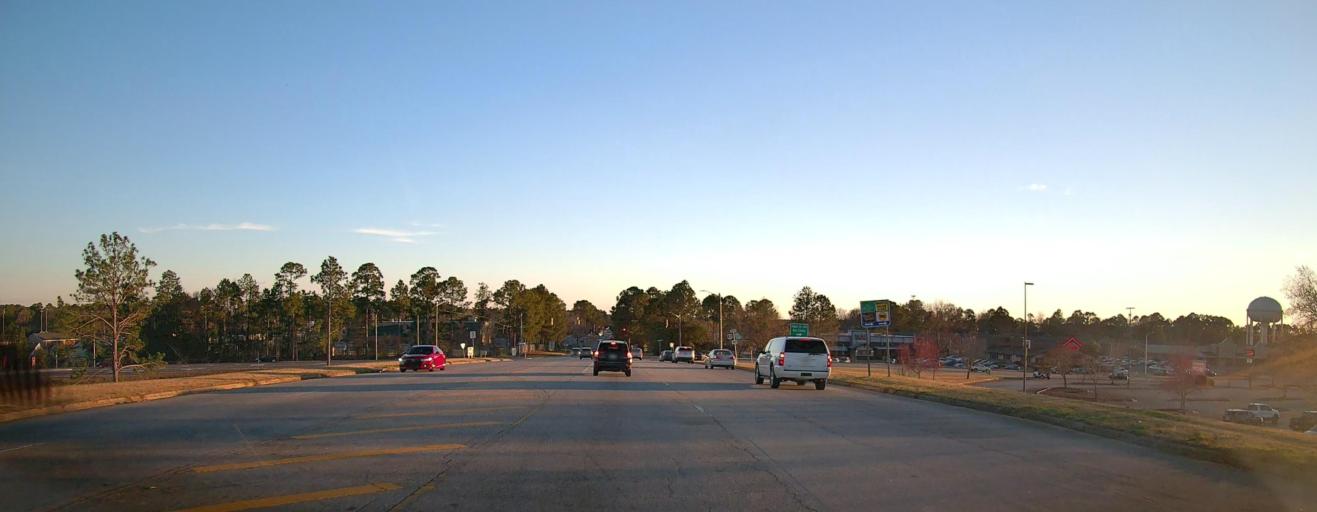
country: US
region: Georgia
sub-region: Dougherty County
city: Albany
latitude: 31.6166
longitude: -84.2043
